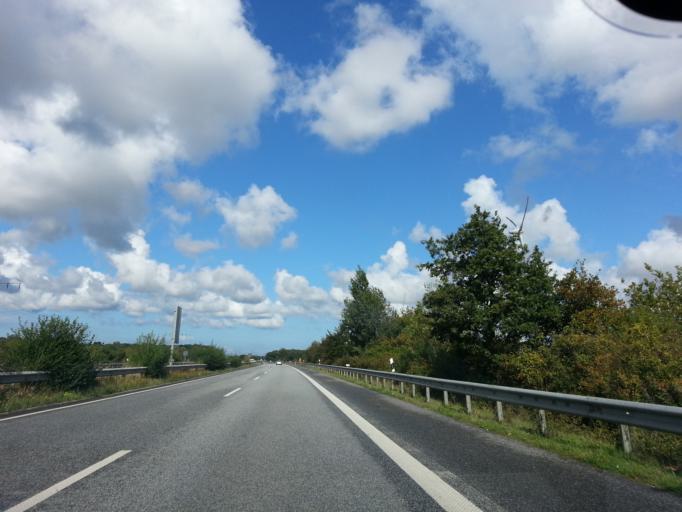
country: DE
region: Schleswig-Holstein
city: Lensahn
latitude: 54.2277
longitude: 10.8996
